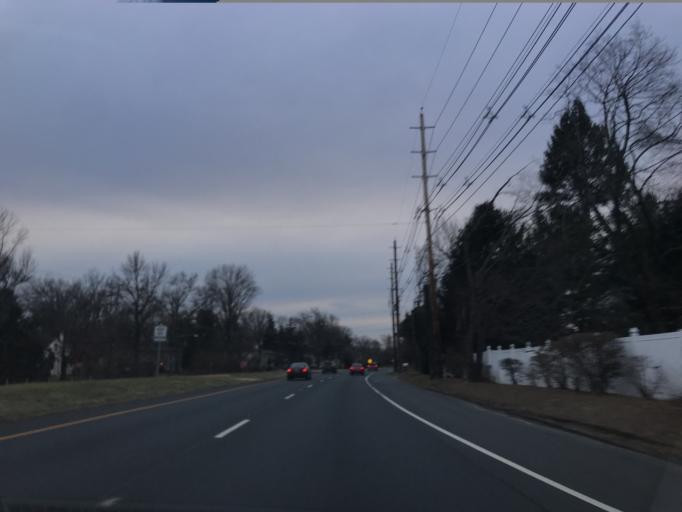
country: US
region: New Jersey
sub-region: Middlesex County
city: Milltown
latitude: 40.4525
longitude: -74.4592
